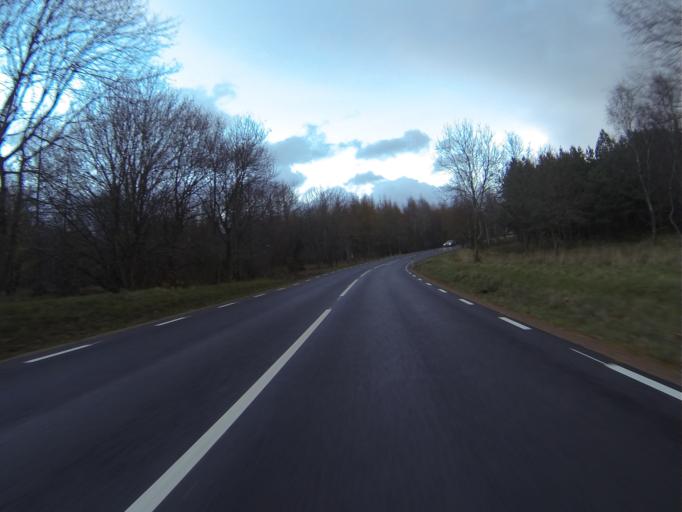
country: SE
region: Skane
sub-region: Lunds Kommun
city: Genarp
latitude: 55.5954
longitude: 13.4139
